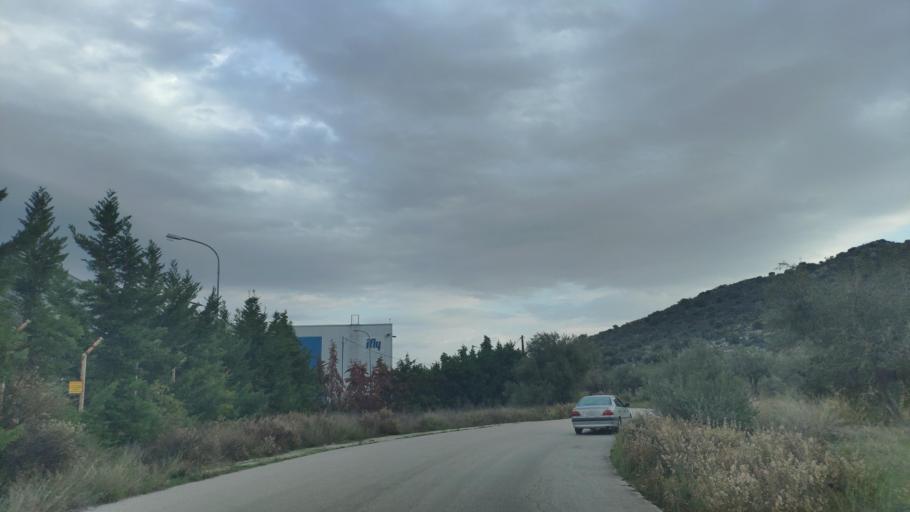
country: GR
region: Attica
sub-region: Nomarchia Dytikis Attikis
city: Megara
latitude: 37.9792
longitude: 23.3756
